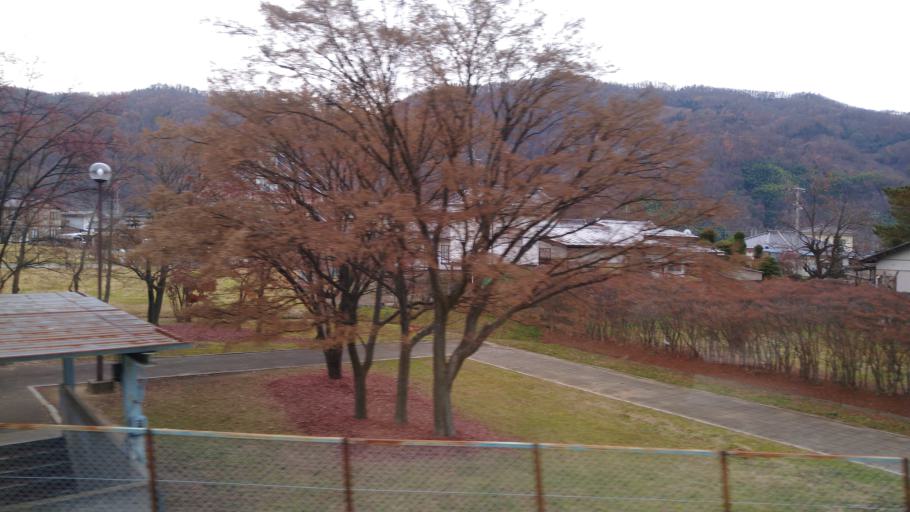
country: JP
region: Nagano
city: Ueda
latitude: 36.3803
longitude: 138.2702
